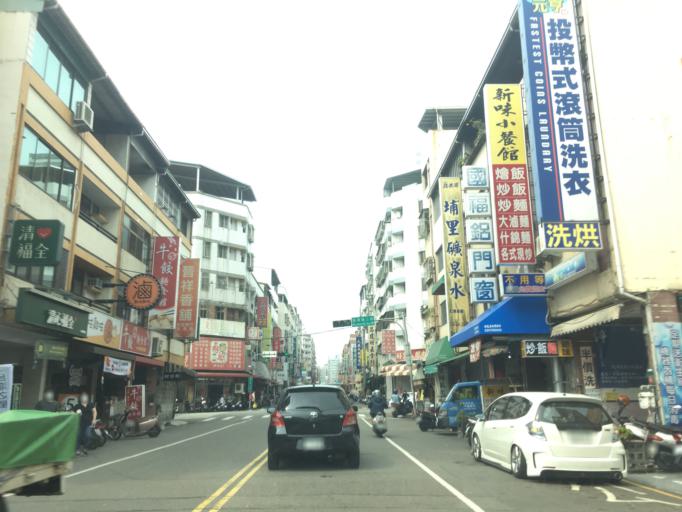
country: TW
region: Taiwan
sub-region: Taichung City
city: Taichung
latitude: 24.1731
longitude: 120.6944
